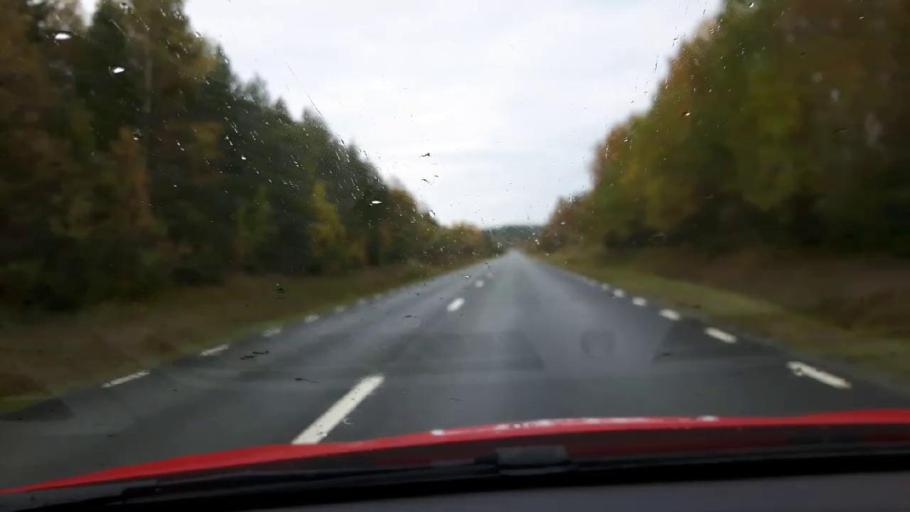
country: SE
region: Jaemtland
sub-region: Krokoms Kommun
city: Krokom
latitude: 63.0856
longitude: 14.2958
